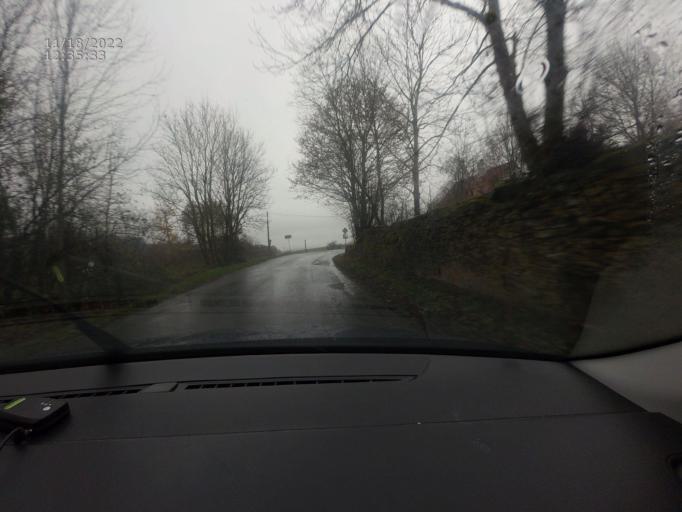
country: CZ
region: Plzensky
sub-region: Okres Klatovy
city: Planice
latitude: 49.4104
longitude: 13.5117
